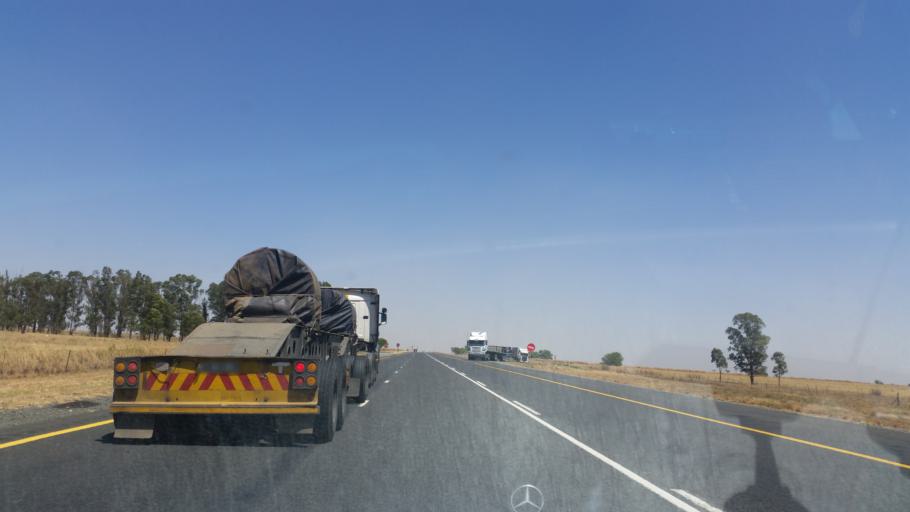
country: ZA
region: Orange Free State
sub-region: Lejweleputswa District Municipality
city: Winburg
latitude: -28.6412
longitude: 26.8894
